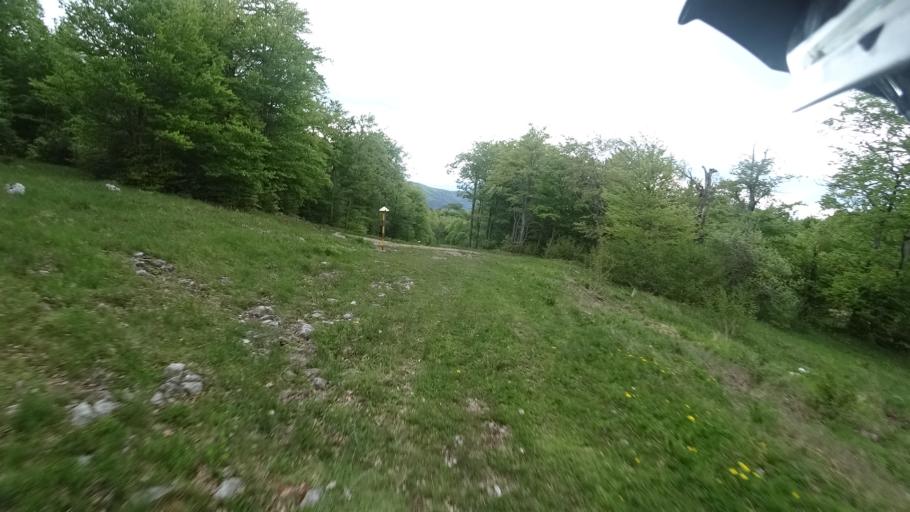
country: HR
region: Karlovacka
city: Plaski
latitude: 44.9081
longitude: 15.4192
